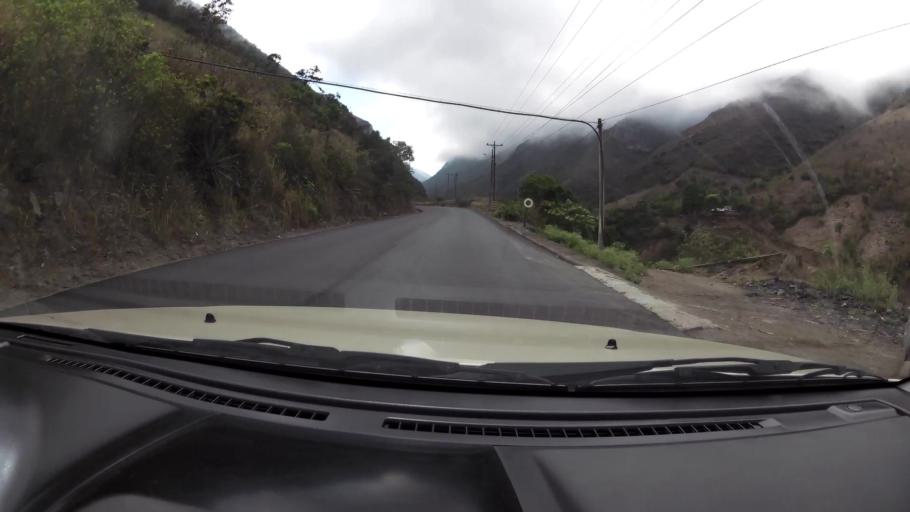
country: EC
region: El Oro
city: Pasaje
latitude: -3.3097
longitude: -79.5079
